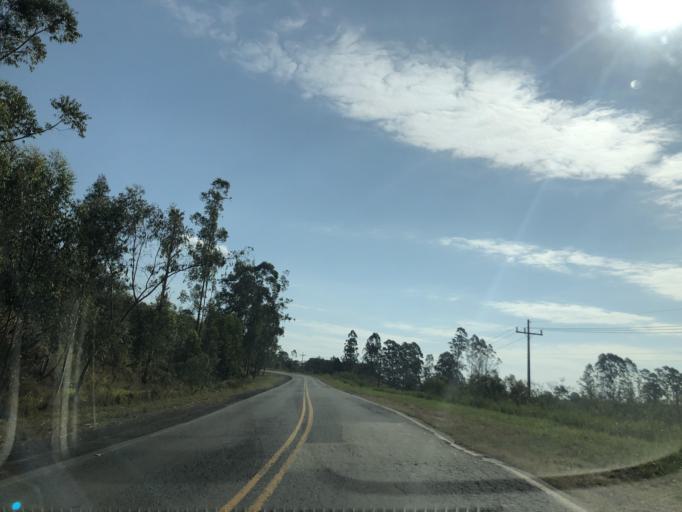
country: BR
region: Sao Paulo
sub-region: Pilar Do Sul
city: Pilar do Sul
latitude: -23.8292
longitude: -47.6699
